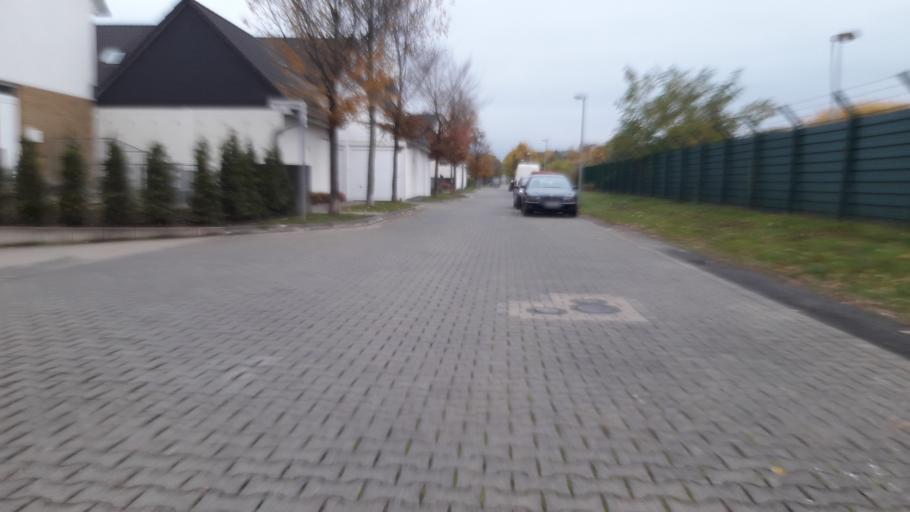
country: DE
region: North Rhine-Westphalia
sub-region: Regierungsbezirk Detmold
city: Paderborn
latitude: 51.7242
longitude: 8.7868
